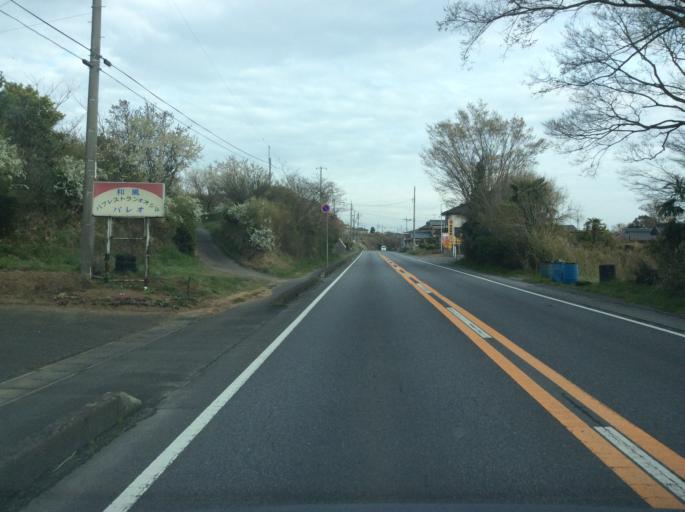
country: JP
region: Ibaraki
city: Tsukuba
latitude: 36.1546
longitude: 140.1139
